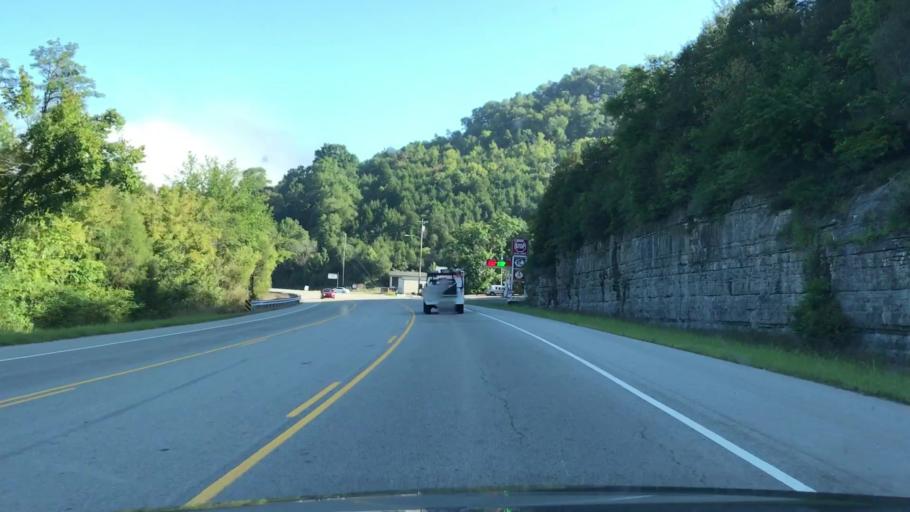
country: US
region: Tennessee
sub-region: Jackson County
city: Gainesboro
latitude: 36.3664
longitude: -85.6513
